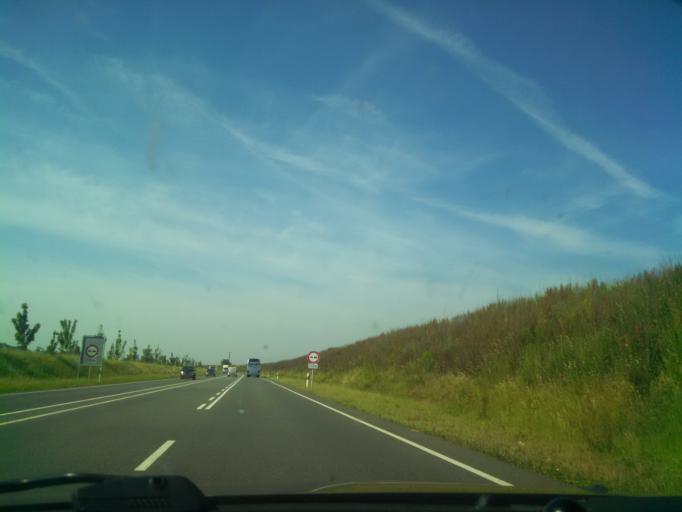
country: LU
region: Grevenmacher
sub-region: Canton de Grevenmacher
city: Junglinster
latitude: 49.7144
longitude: 6.2682
